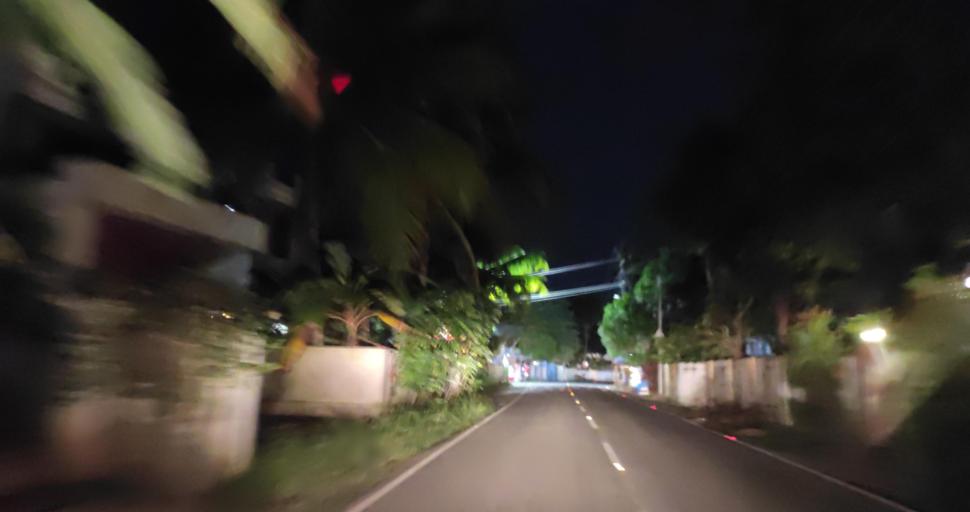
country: IN
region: Kerala
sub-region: Alappuzha
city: Vayalar
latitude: 9.6810
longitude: 76.3252
